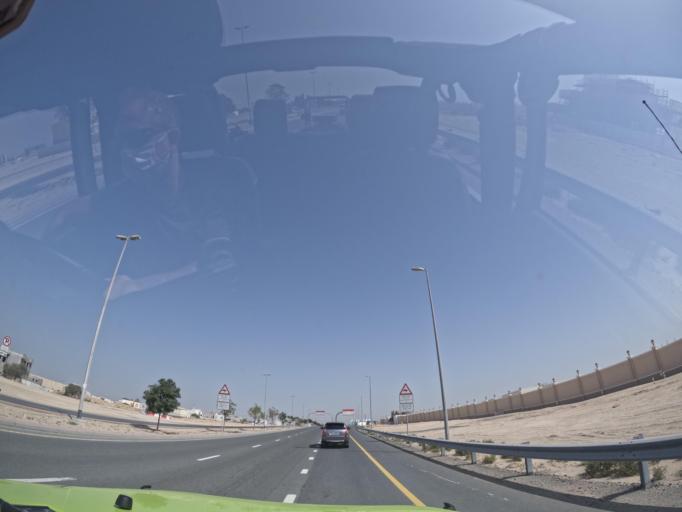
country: AE
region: Ash Shariqah
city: Sharjah
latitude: 25.1551
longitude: 55.3627
